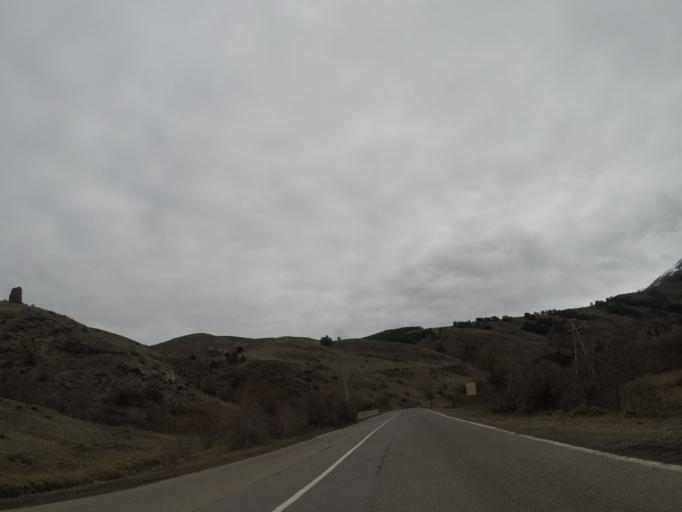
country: GE
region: Samtskhe-Javakheti
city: Aspindza
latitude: 41.6146
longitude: 43.1381
